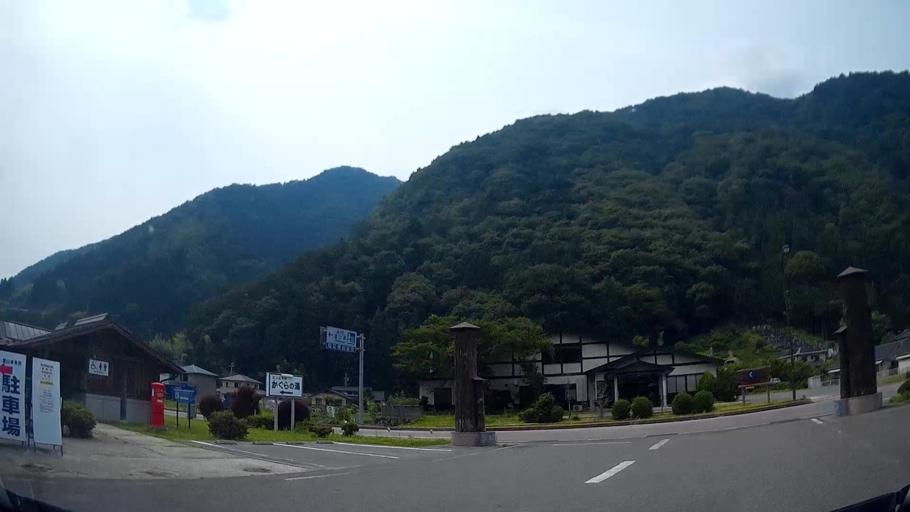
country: JP
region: Nagano
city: Iida
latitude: 35.3213
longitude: 137.9295
